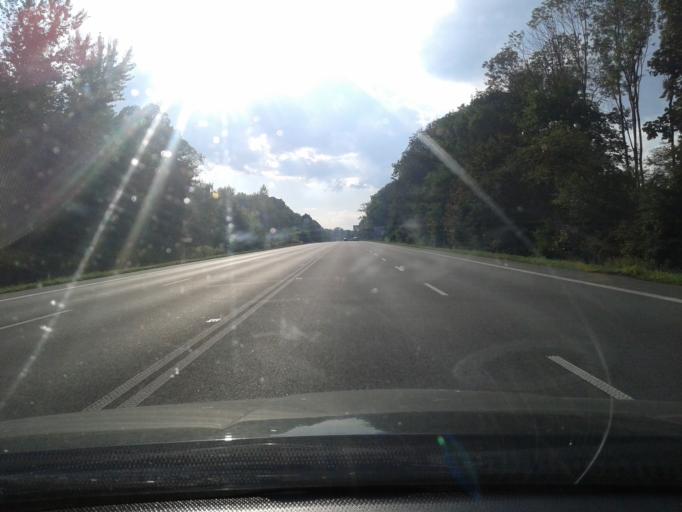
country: CZ
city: Vratimov
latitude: 49.8054
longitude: 18.3178
